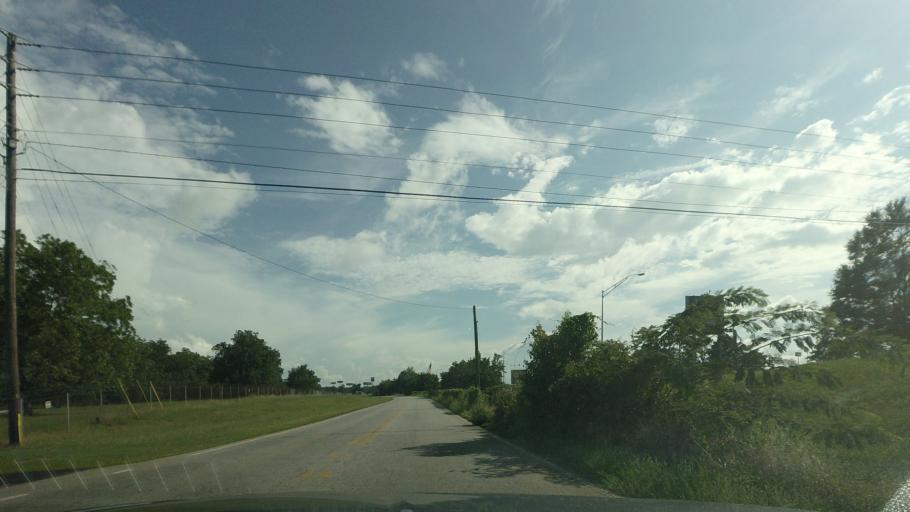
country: US
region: Georgia
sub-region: Peach County
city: Byron
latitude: 32.6587
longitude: -83.7434
